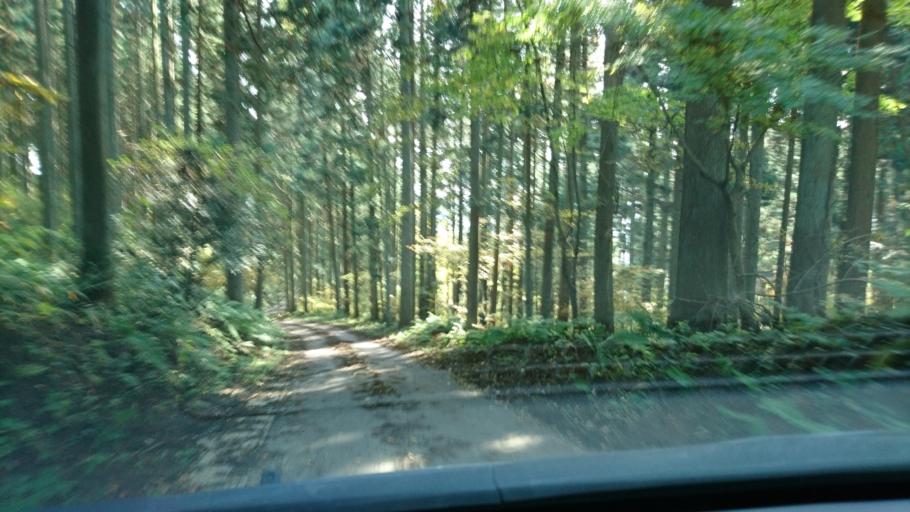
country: JP
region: Iwate
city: Ichinoseki
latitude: 38.9842
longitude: 141.1711
